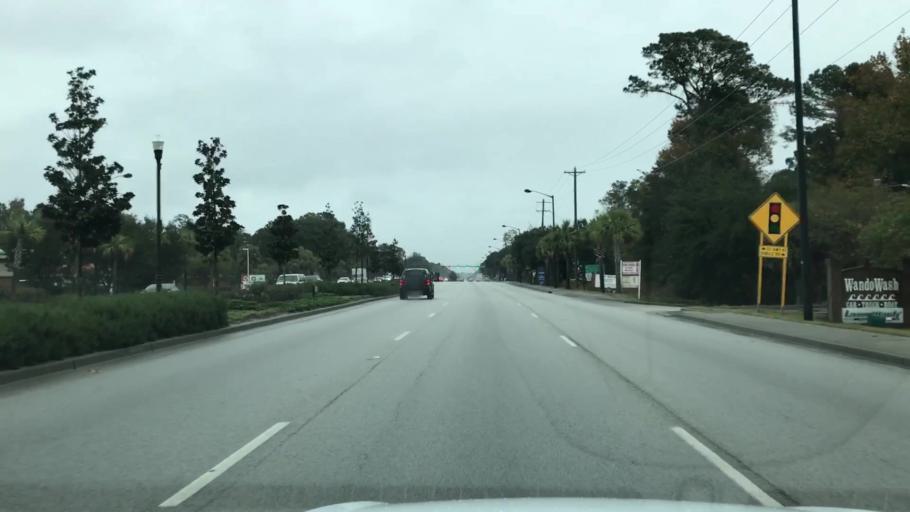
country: US
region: South Carolina
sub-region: Charleston County
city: Isle of Palms
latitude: 32.8571
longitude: -79.7977
